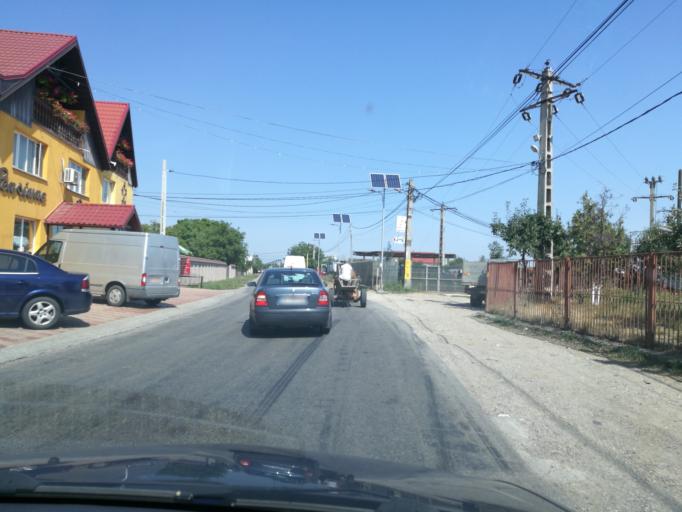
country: RO
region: Bacau
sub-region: Comuna Margineni
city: Margineni
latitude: 46.5872
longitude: 26.8643
